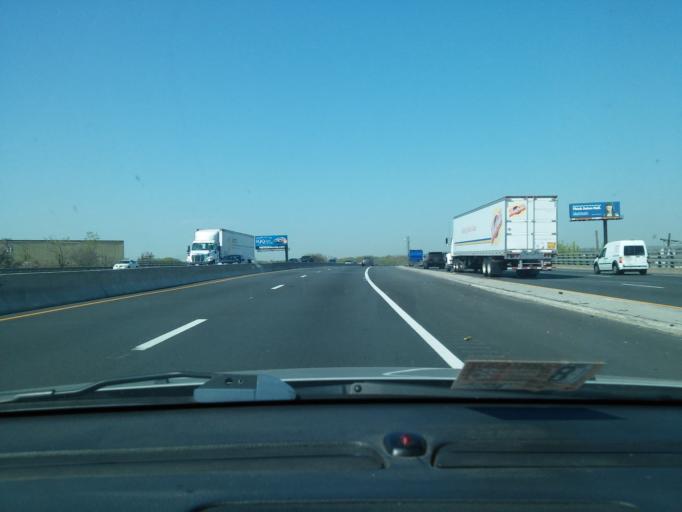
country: US
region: New Jersey
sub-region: Union County
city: Hillside
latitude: 40.7057
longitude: -74.2371
